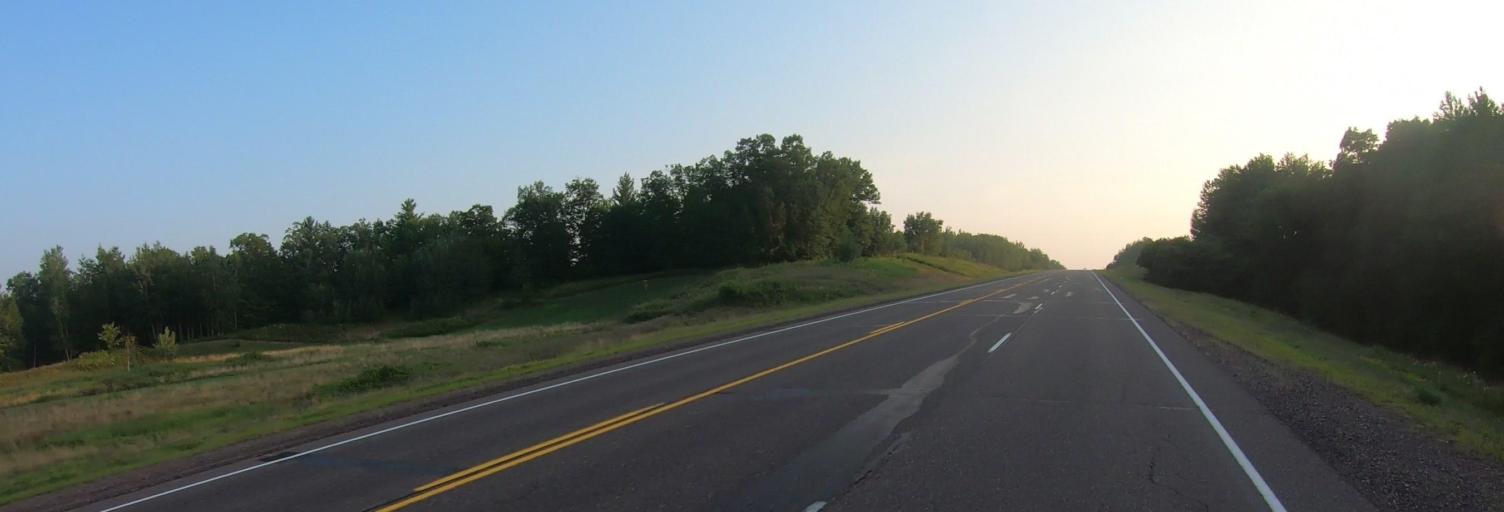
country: US
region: Wisconsin
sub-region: Burnett County
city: Siren
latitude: 45.7822
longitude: -92.4256
